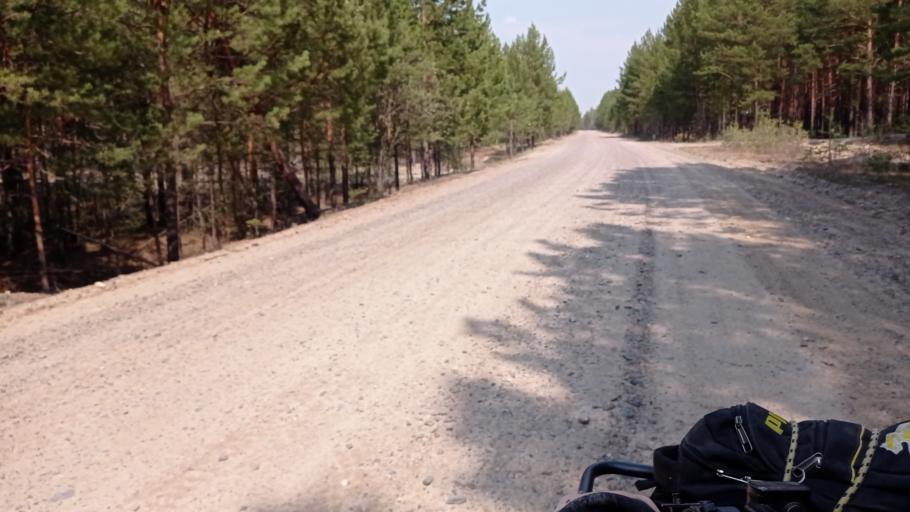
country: RU
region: Tomsk
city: Timiryazevskoye
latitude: 56.4175
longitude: 84.6707
